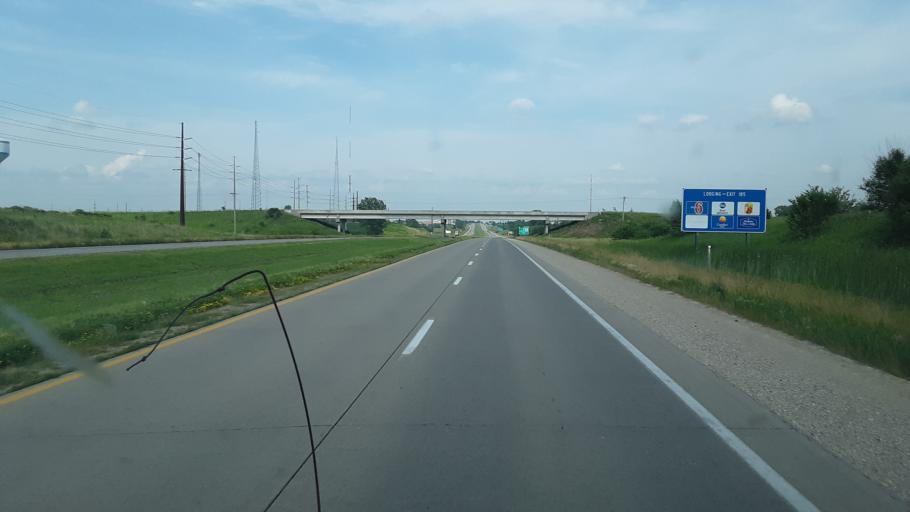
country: US
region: Iowa
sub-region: Marshall County
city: Marshalltown
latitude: 42.0033
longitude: -92.9441
